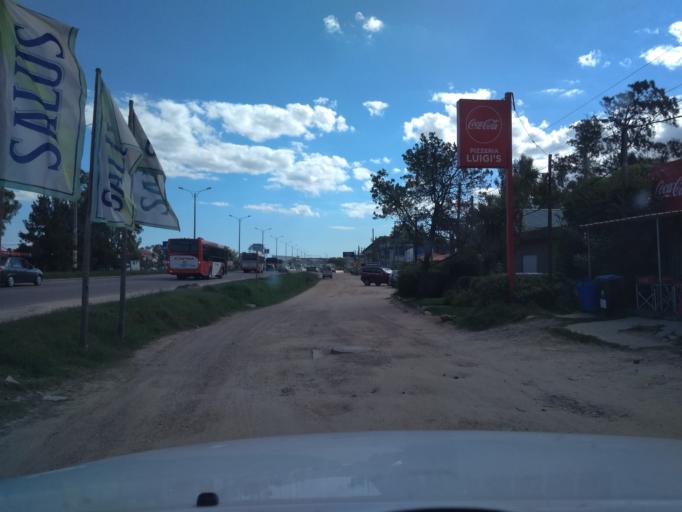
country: UY
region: Canelones
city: Barra de Carrasco
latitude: -34.8363
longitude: -55.9850
